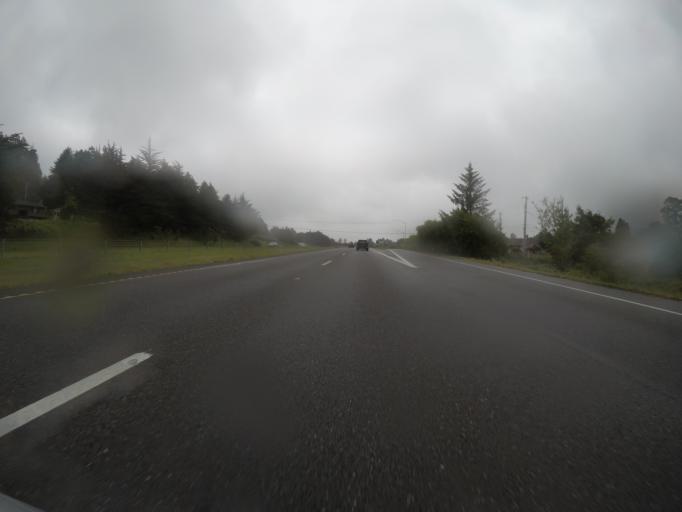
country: US
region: California
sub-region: Humboldt County
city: Arcata
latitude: 40.8827
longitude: -124.0811
